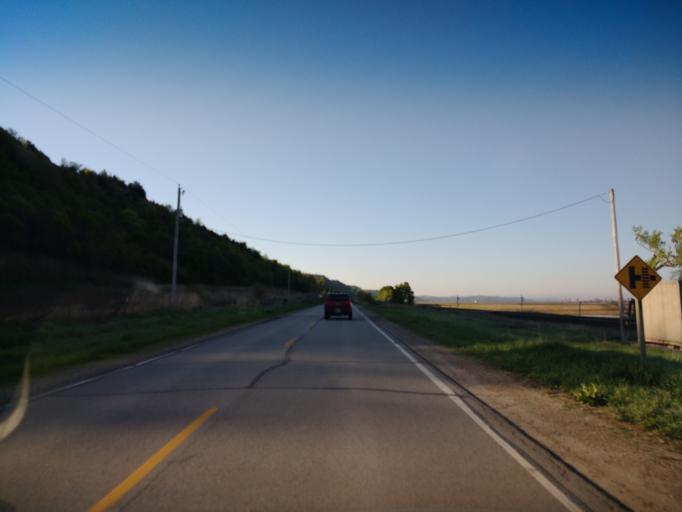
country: US
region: Iowa
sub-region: Harrison County
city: Missouri Valley
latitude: 41.4891
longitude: -95.8882
